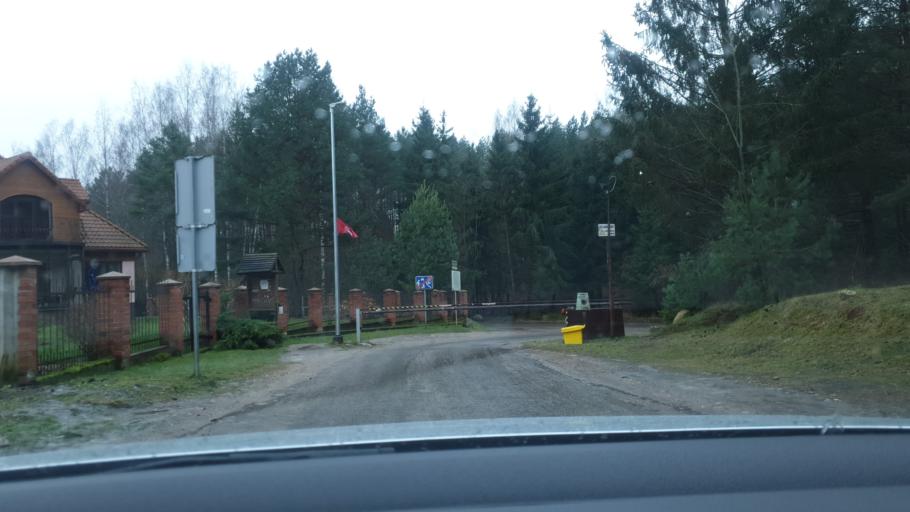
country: LT
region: Vilnius County
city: Rasos
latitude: 54.7186
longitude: 25.3805
